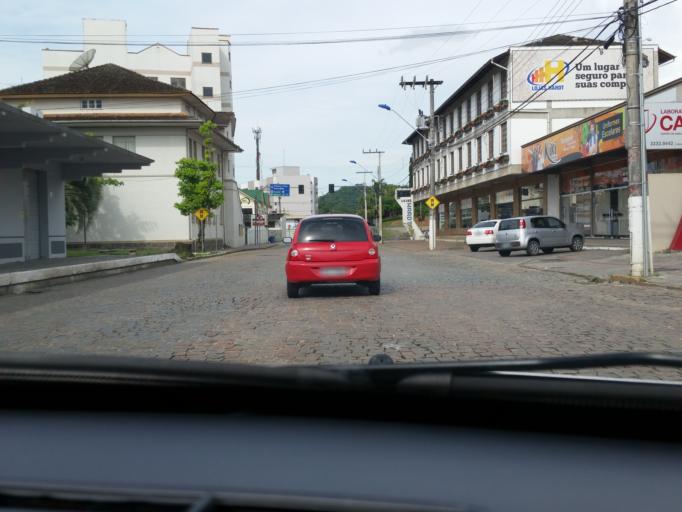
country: BR
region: Santa Catarina
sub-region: Indaial
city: Indaial
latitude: -26.8976
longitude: -49.2357
